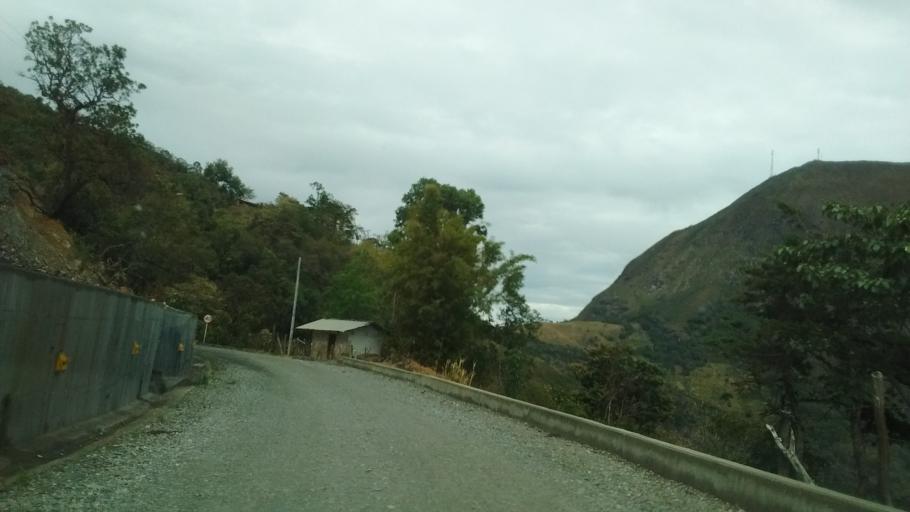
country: CO
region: Cauca
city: Almaguer
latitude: 1.8568
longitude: -76.9422
